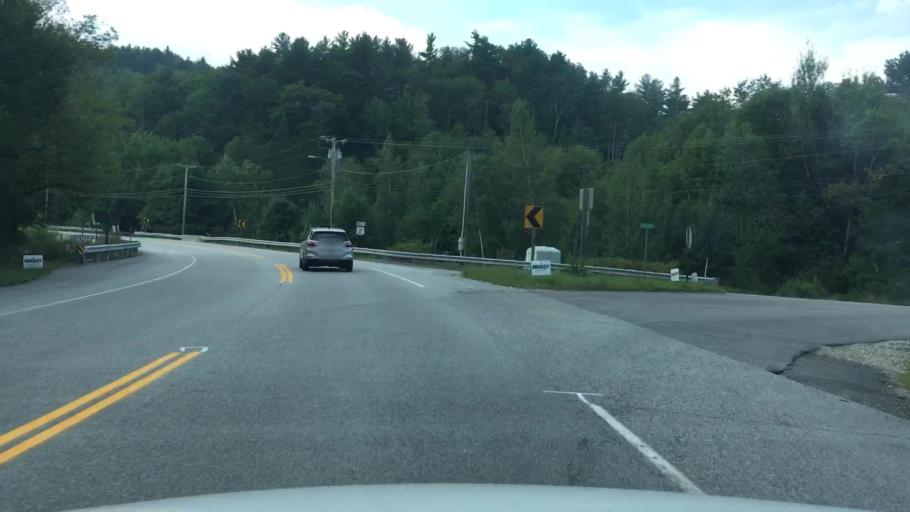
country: US
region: Maine
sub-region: Oxford County
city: Rumford
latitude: 44.5131
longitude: -70.6191
